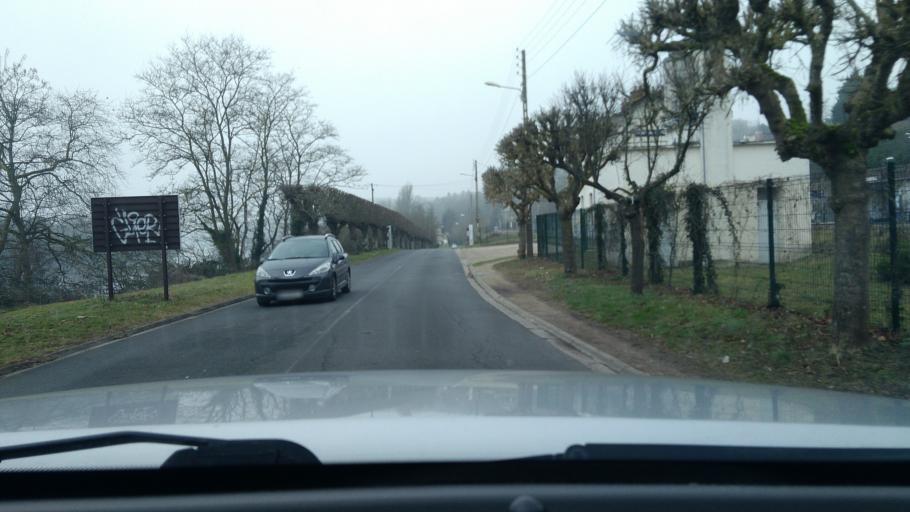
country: FR
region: Ile-de-France
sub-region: Departement de Seine-et-Marne
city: Samois-sur-Seine
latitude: 48.4868
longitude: 2.7519
